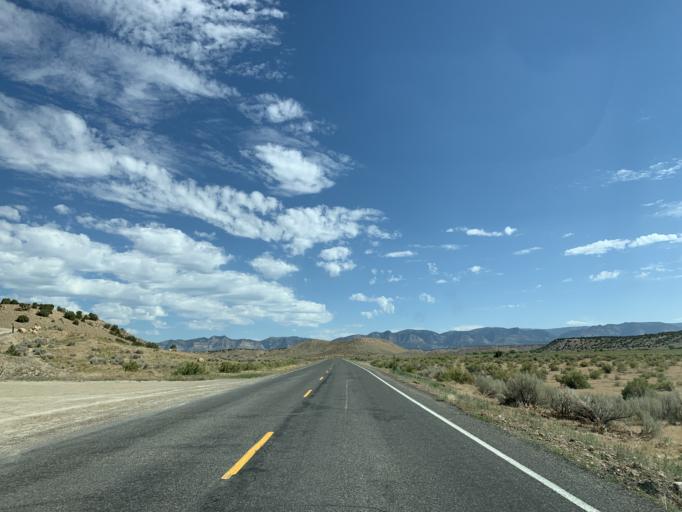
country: US
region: Utah
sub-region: Carbon County
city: Wellington
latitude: 39.5759
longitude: -110.6527
